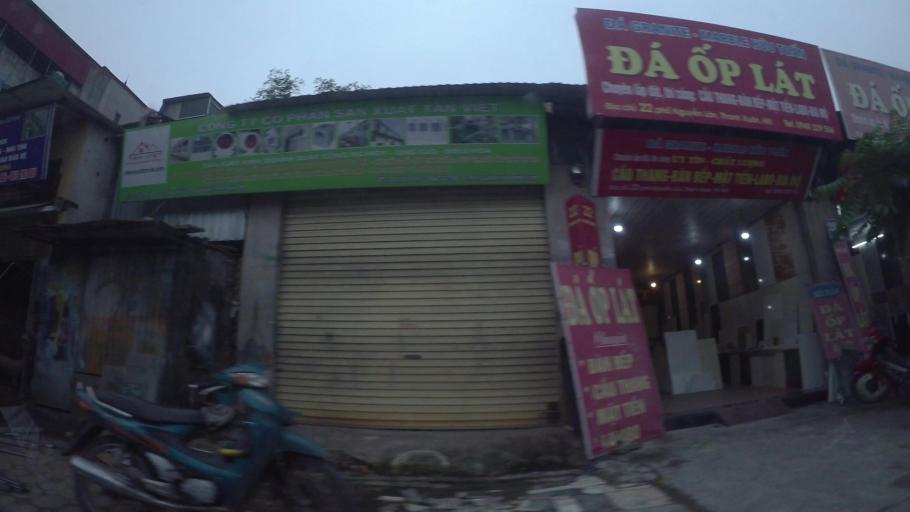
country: VN
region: Ha Noi
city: Hai BaTrung
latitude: 20.9967
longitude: 105.8362
